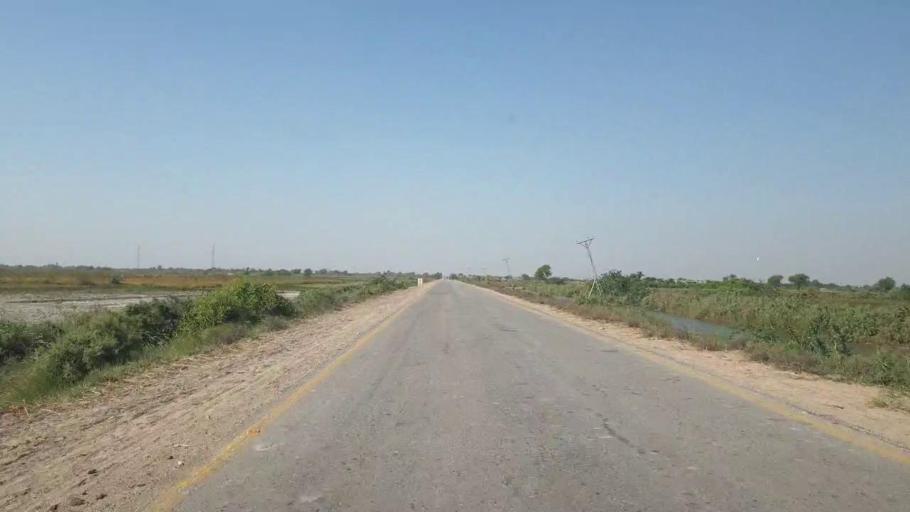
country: PK
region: Sindh
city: Rajo Khanani
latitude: 25.0527
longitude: 68.8064
